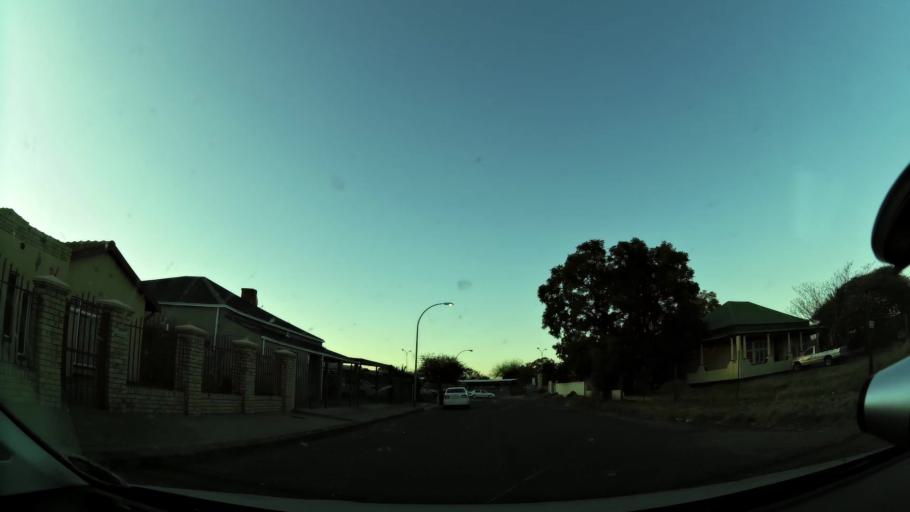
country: ZA
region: Northern Cape
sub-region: Frances Baard District Municipality
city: Kimberley
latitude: -28.7334
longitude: 24.7676
